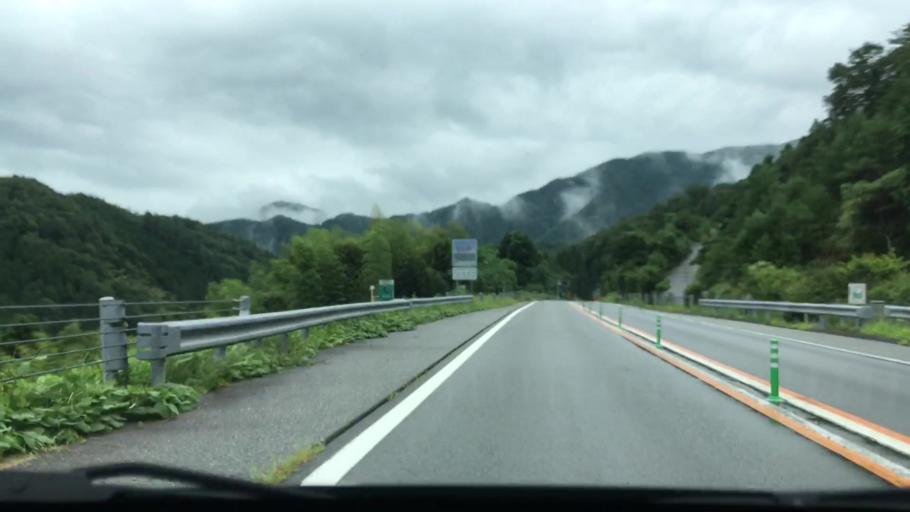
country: JP
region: Hyogo
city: Toyooka
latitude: 35.2450
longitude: 134.7894
